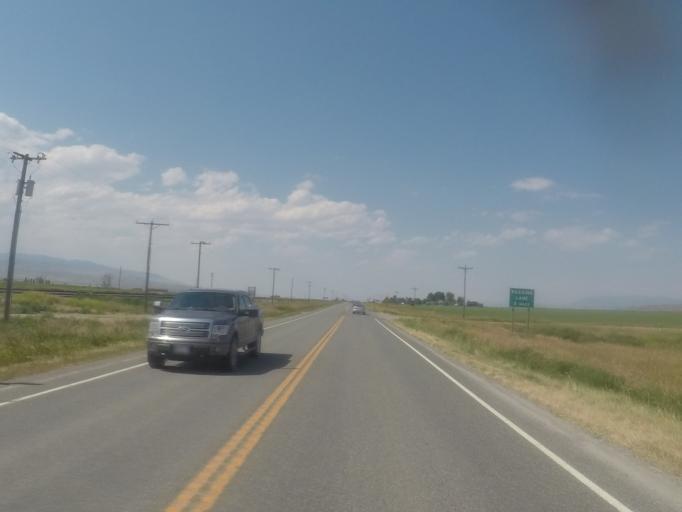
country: US
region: Montana
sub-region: Broadwater County
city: Townsend
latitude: 46.1810
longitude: -111.4447
